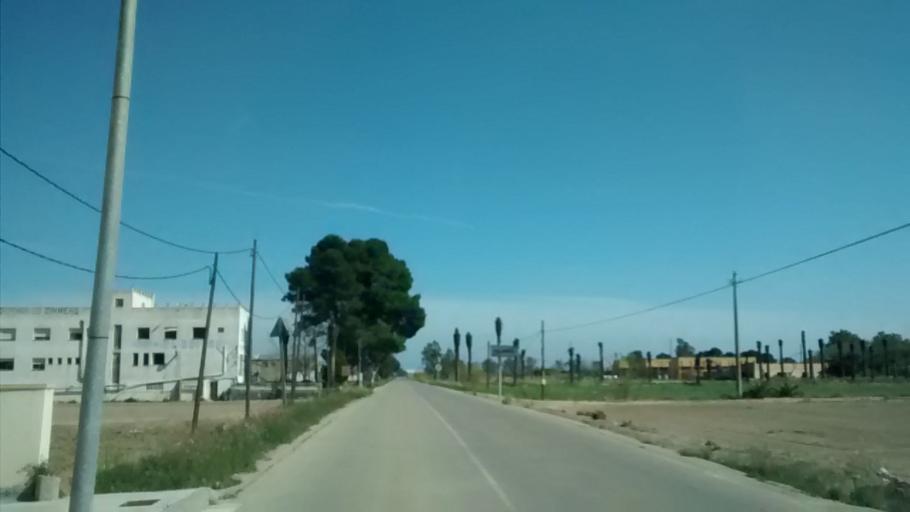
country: ES
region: Catalonia
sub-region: Provincia de Tarragona
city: Deltebre
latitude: 40.7142
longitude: 0.7497
